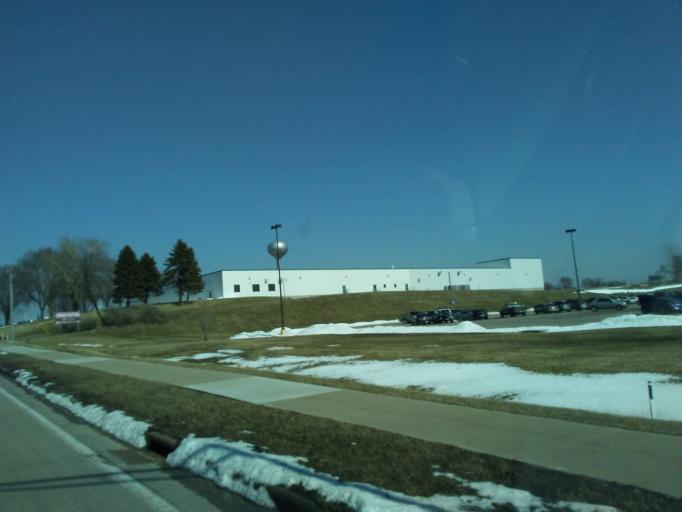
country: US
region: Wisconsin
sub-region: Vernon County
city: Viroqua
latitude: 43.5702
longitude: -90.8888
